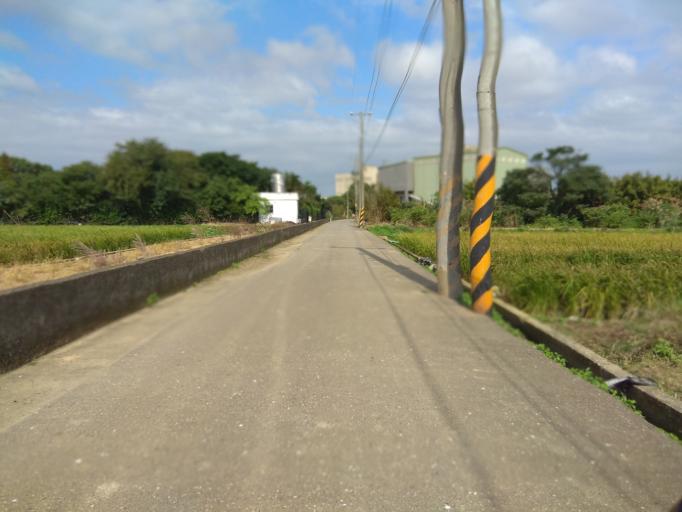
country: TW
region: Taiwan
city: Taoyuan City
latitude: 25.0740
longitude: 121.2489
